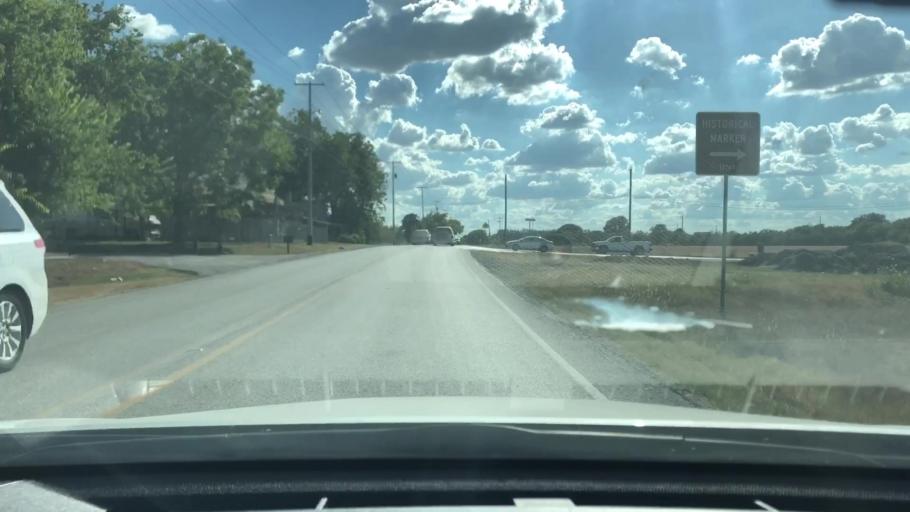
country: US
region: Texas
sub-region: Guadalupe County
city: Northcliff
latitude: 29.6458
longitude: -98.2226
